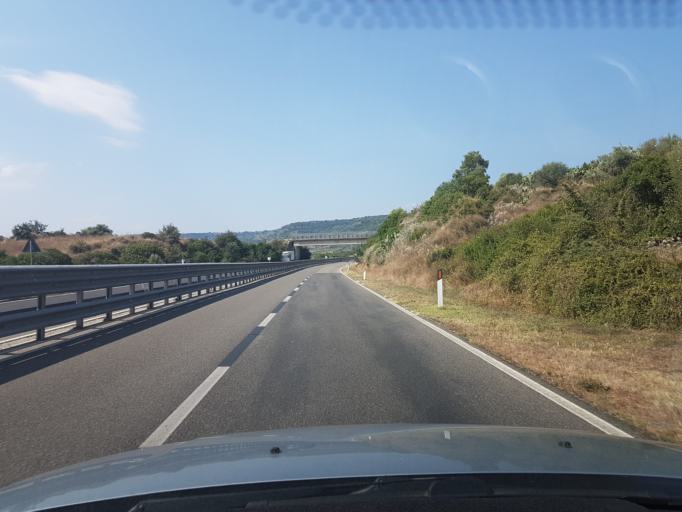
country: IT
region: Sardinia
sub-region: Provincia di Oristano
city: Sedilo
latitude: 40.1533
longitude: 8.9023
